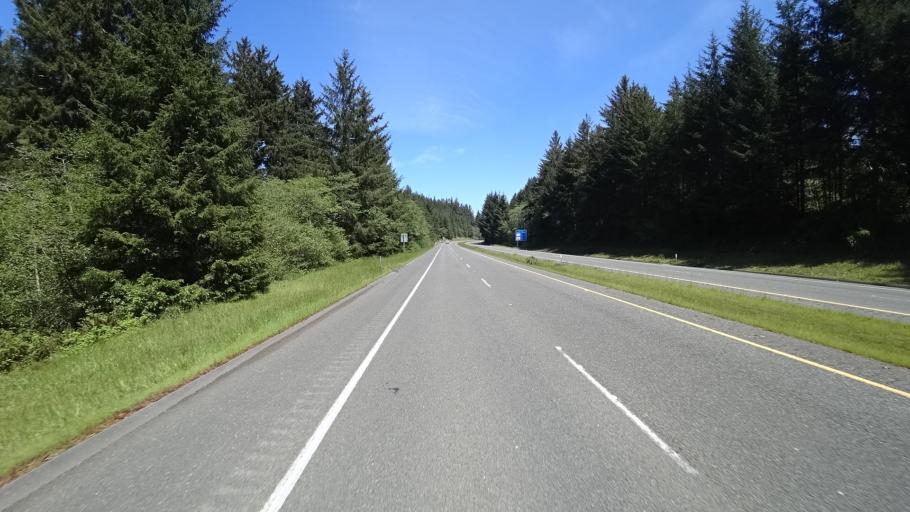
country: US
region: California
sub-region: Humboldt County
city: Westhaven-Moonstone
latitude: 41.1292
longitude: -124.1507
